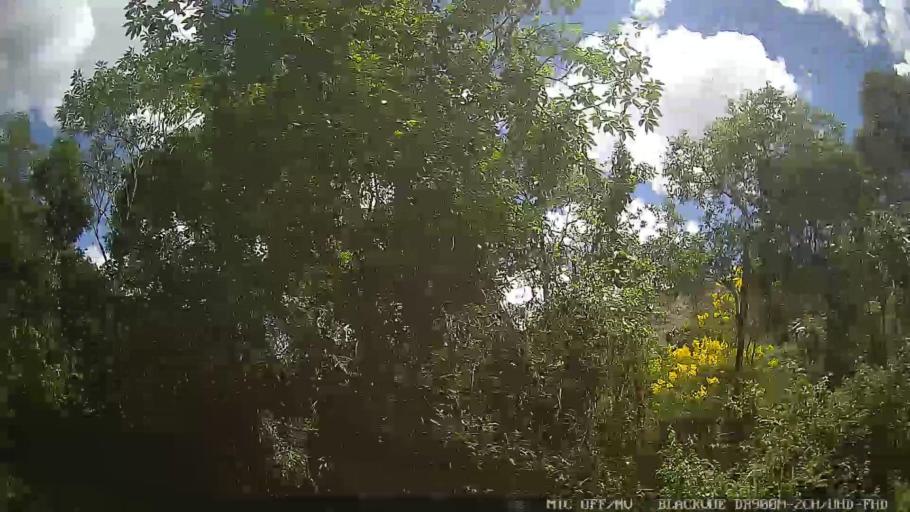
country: BR
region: Sao Paulo
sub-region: Santa Branca
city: Santa Branca
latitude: -23.5521
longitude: -45.6862
